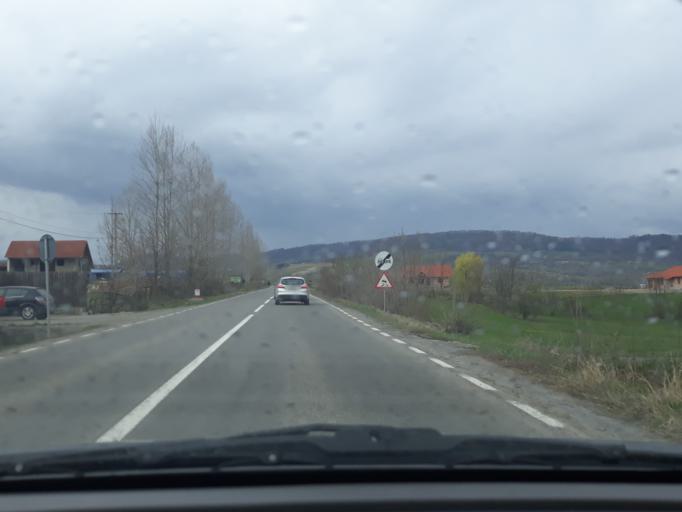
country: RO
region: Harghita
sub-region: Comuna Lupeni
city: Lupeni
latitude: 46.3844
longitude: 25.2182
